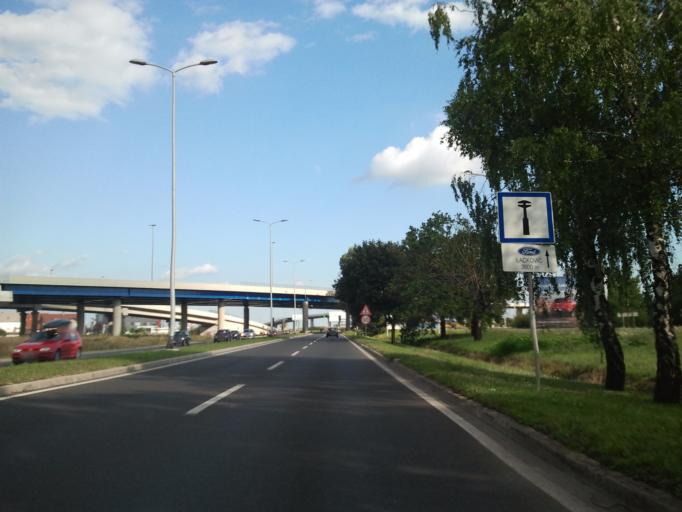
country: HR
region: Grad Zagreb
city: Odra
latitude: 45.7370
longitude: 16.0078
